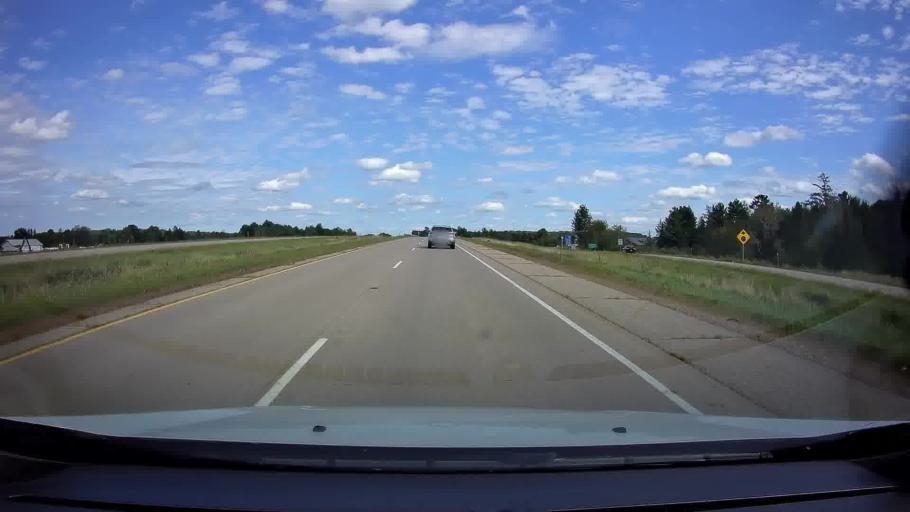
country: US
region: Wisconsin
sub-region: Shawano County
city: Wittenberg
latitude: 44.8234
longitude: -89.1271
